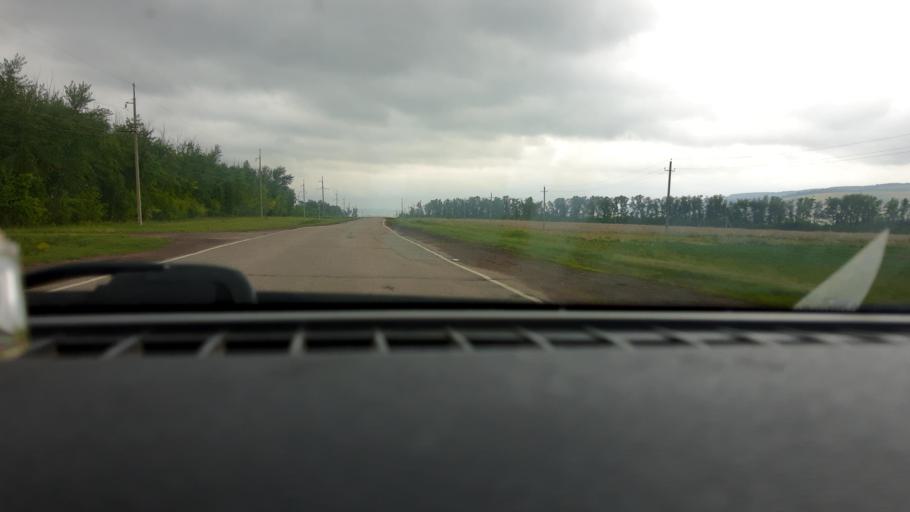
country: RU
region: Bashkortostan
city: Kandry
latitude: 54.3476
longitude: 54.0429
